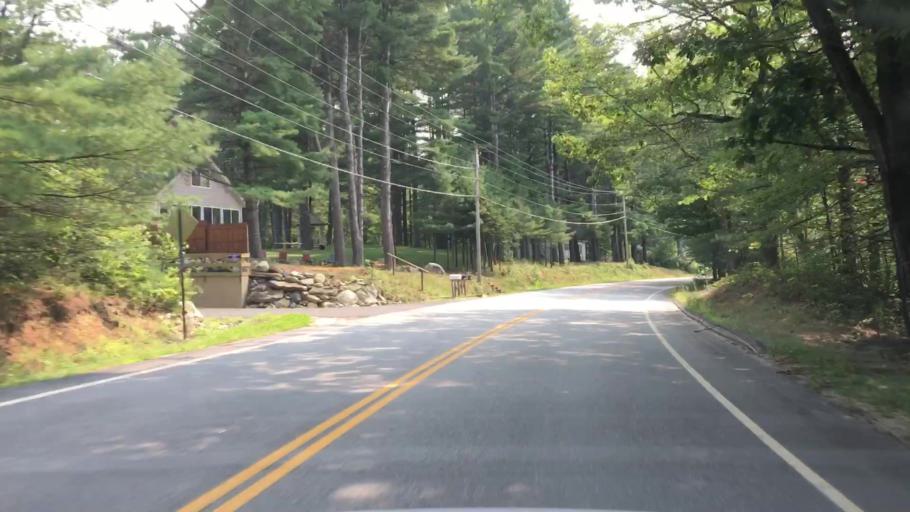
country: US
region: Maine
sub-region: Androscoggin County
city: Livermore
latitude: 44.3383
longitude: -70.2674
